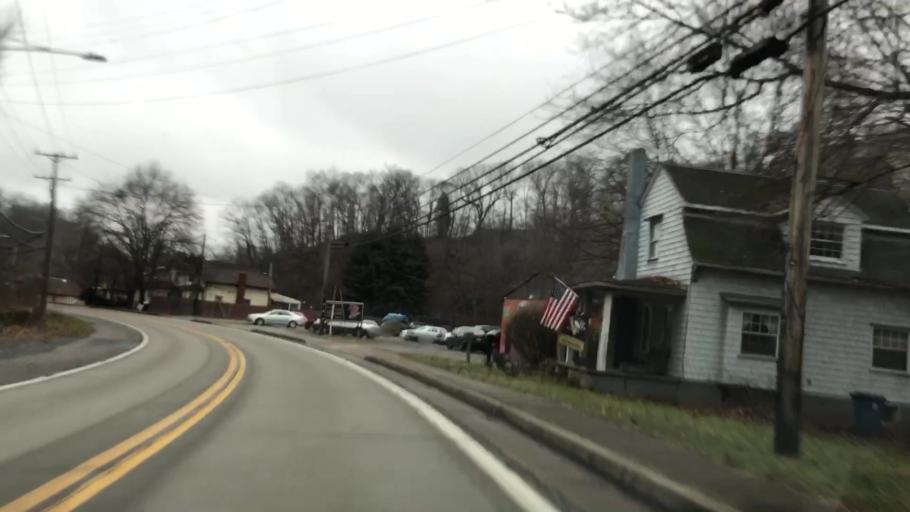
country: US
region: Pennsylvania
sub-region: Allegheny County
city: Leetsdale
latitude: 40.5525
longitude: -80.2190
